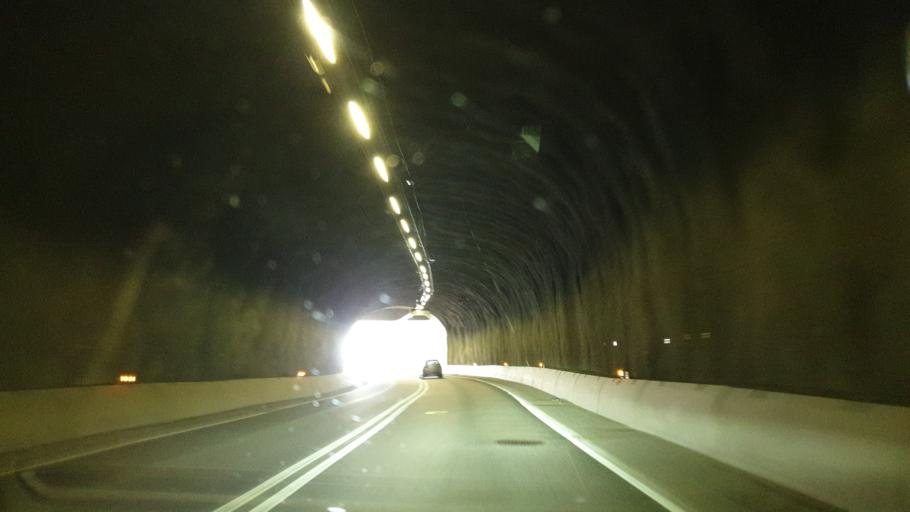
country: SE
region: Stockholm
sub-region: Nacka Kommun
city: Nacka
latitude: 59.3143
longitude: 18.1496
